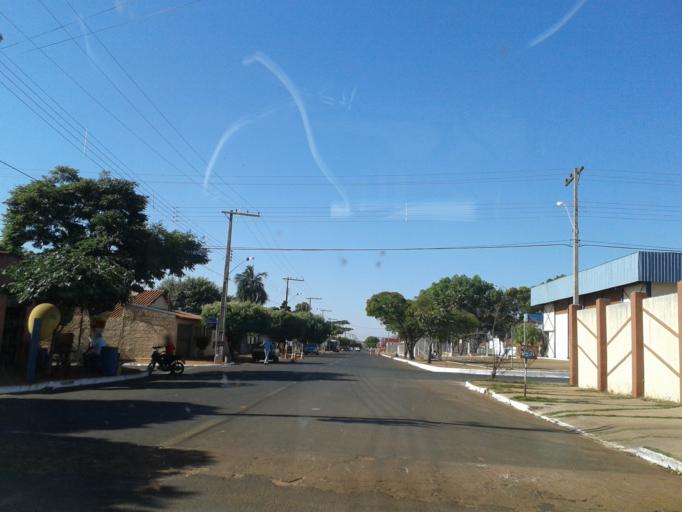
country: BR
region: Minas Gerais
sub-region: Santa Vitoria
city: Santa Vitoria
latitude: -18.8505
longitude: -50.1302
